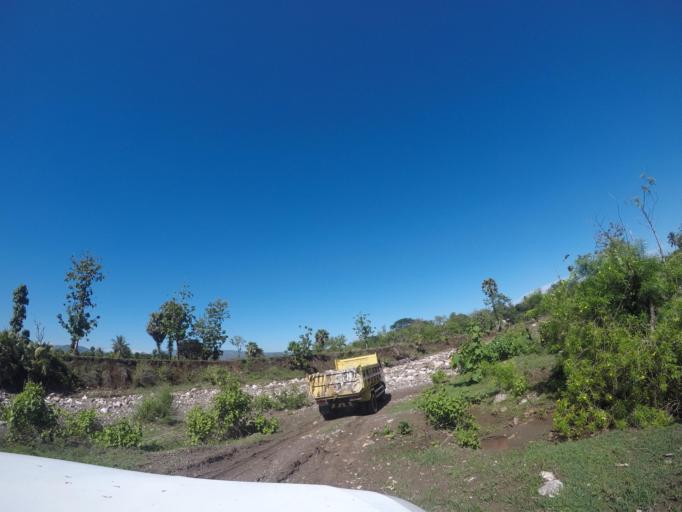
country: TL
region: Bobonaro
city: Maliana
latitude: -8.9911
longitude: 125.2096
